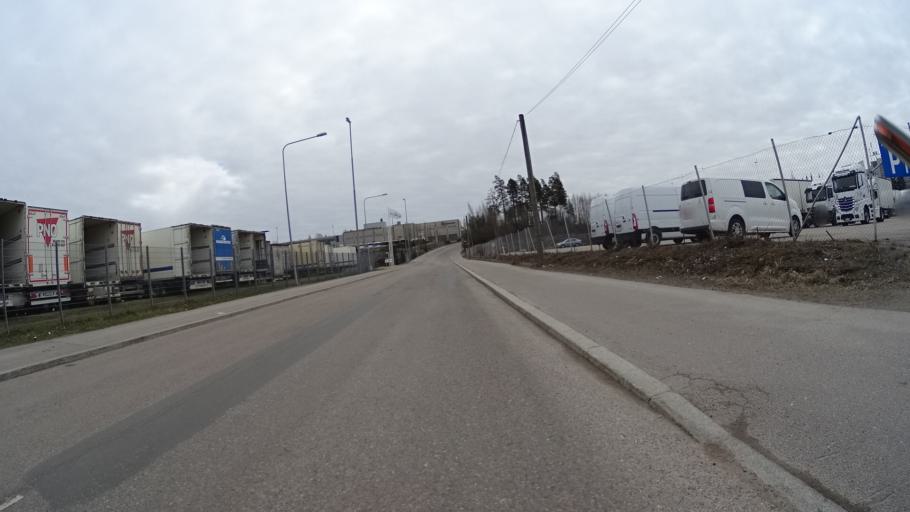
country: FI
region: Uusimaa
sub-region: Helsinki
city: Teekkarikylae
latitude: 60.2992
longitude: 24.9068
